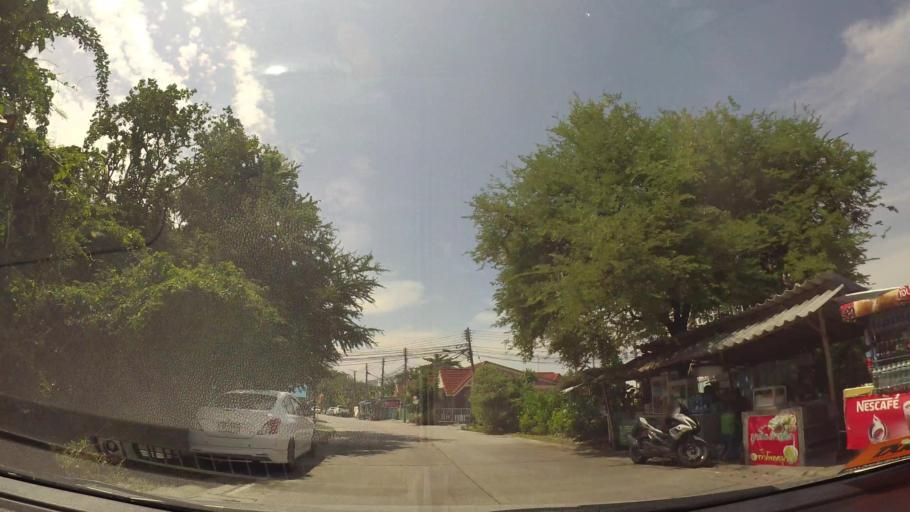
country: TH
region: Chon Buri
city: Chon Buri
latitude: 13.3188
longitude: 100.9549
